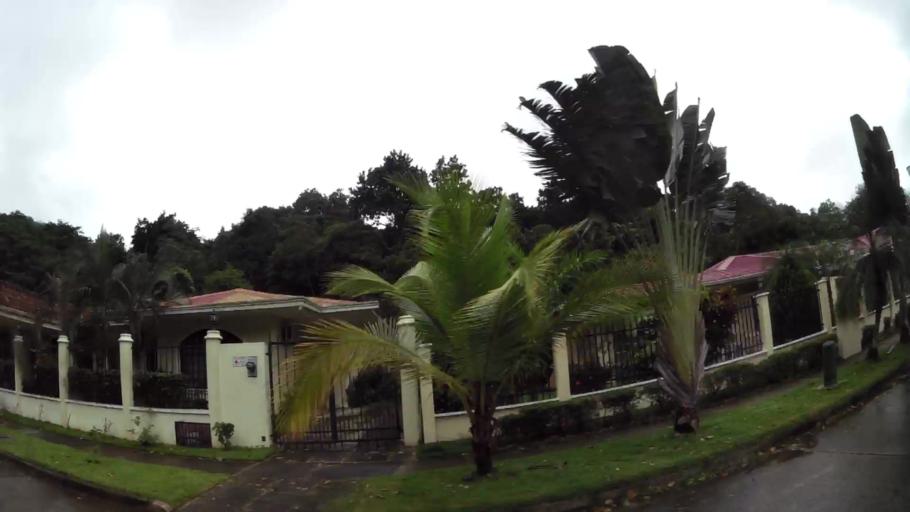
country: PA
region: Panama
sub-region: Distrito de Panama
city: Ancon
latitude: 8.9872
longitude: -79.5618
